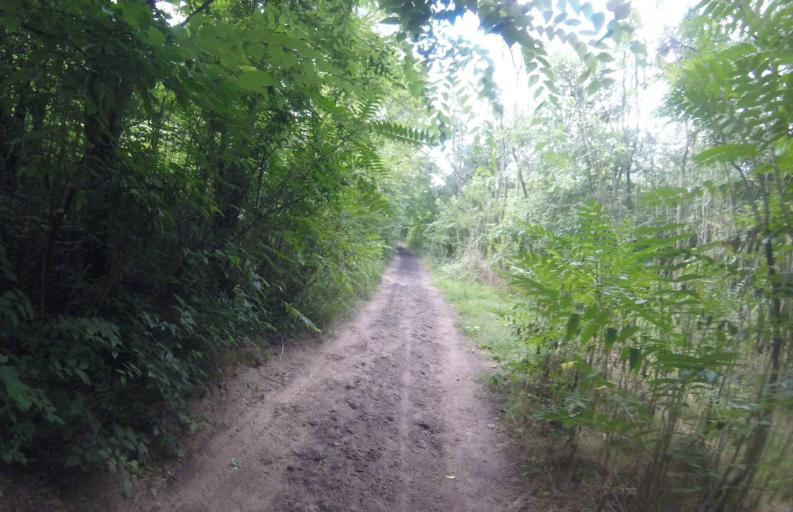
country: HU
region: Pest
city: Fot
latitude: 47.6623
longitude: 19.1850
